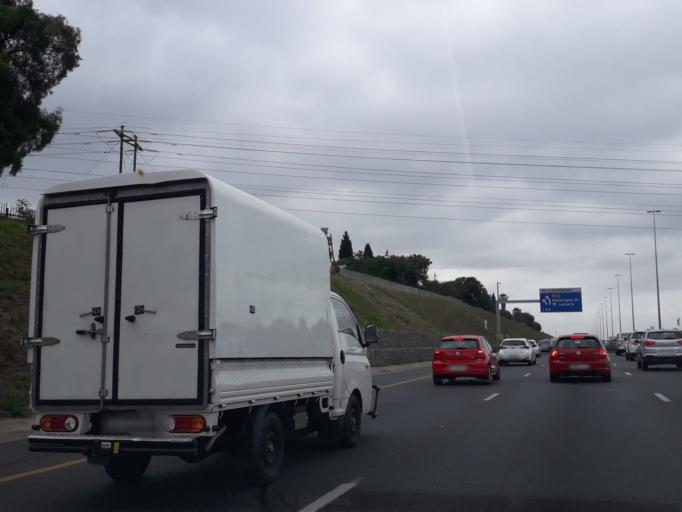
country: ZA
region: Gauteng
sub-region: City of Johannesburg Metropolitan Municipality
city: Roodepoort
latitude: -26.0875
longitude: 27.9686
